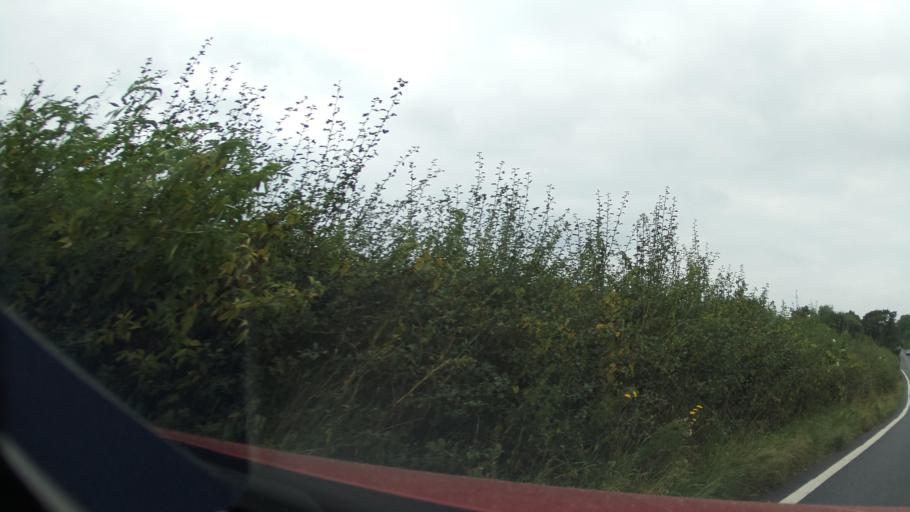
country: GB
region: England
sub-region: Derbyshire
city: Duffield
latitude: 53.0089
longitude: -1.5351
